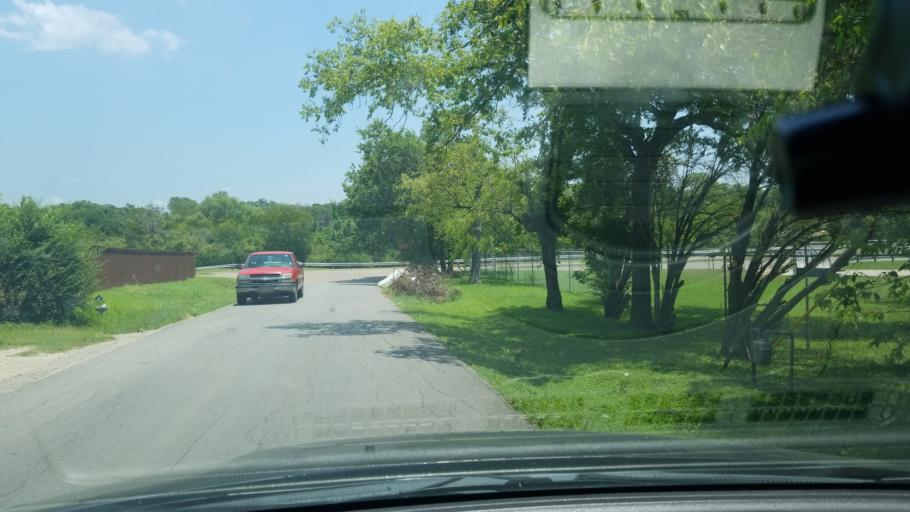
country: US
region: Texas
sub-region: Dallas County
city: Balch Springs
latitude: 32.7253
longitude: -96.6669
